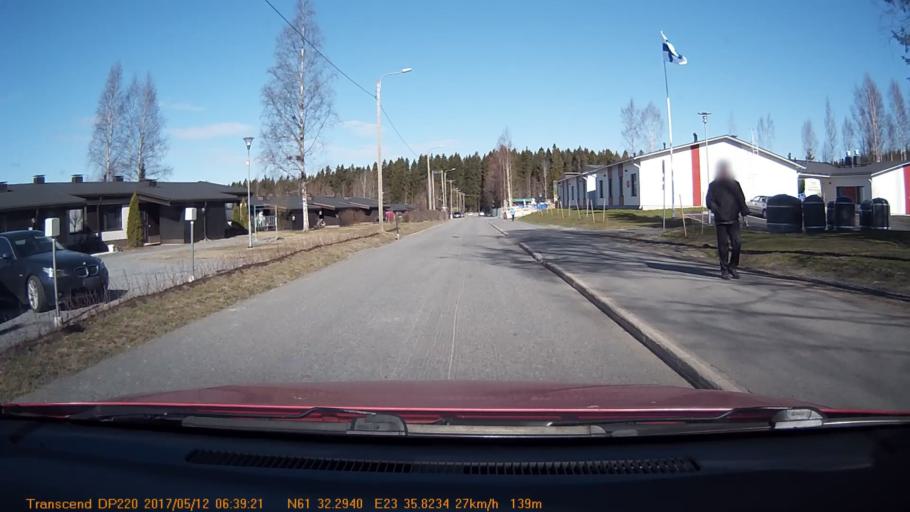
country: FI
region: Pirkanmaa
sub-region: Tampere
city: Yloejaervi
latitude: 61.5382
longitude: 23.5972
